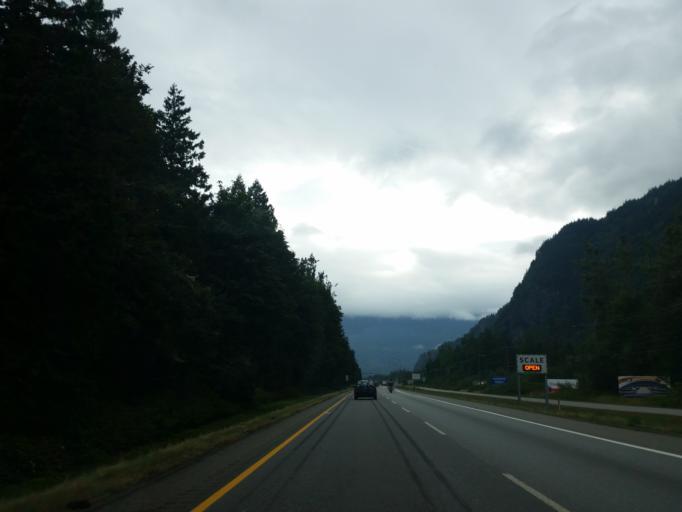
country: CA
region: British Columbia
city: Hope
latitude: 49.3371
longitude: -121.6028
